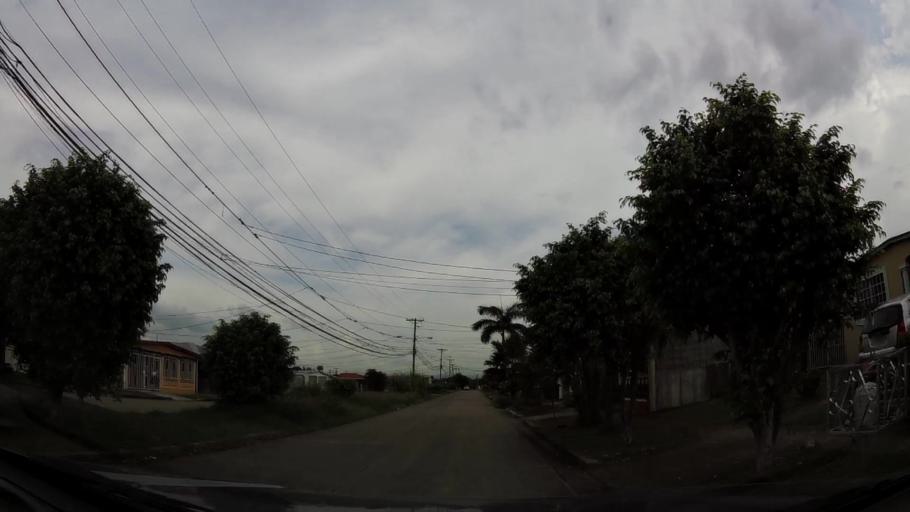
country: PA
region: Panama
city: Cabra Numero Uno
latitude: 9.0936
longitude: -79.3498
